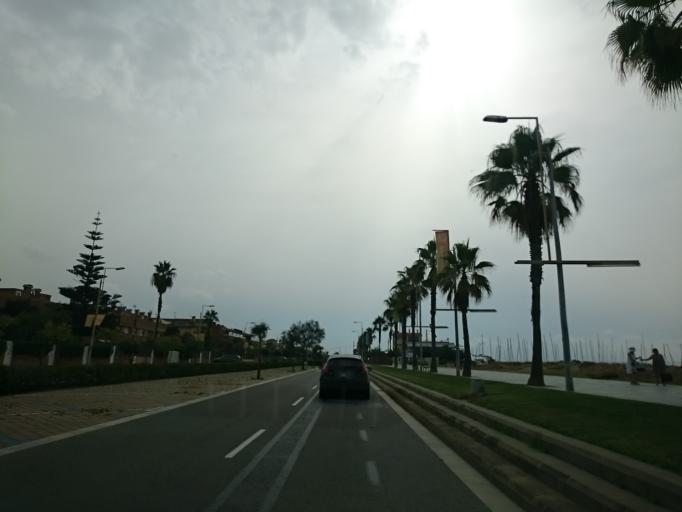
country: ES
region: Catalonia
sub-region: Provincia de Barcelona
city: Castelldefels
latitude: 41.2652
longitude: 1.9952
